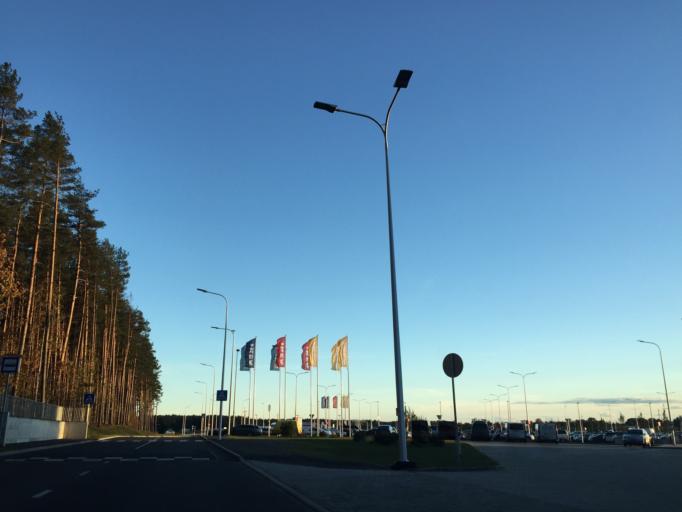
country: LV
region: Stopini
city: Ulbroka
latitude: 56.9547
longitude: 24.2571
